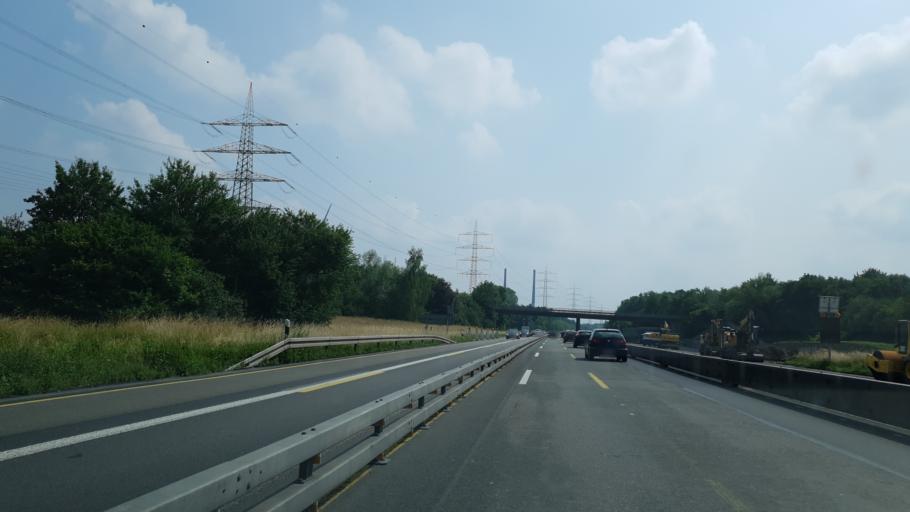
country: DE
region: North Rhine-Westphalia
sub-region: Regierungsbezirk Munster
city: Gladbeck
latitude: 51.5872
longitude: 6.9393
